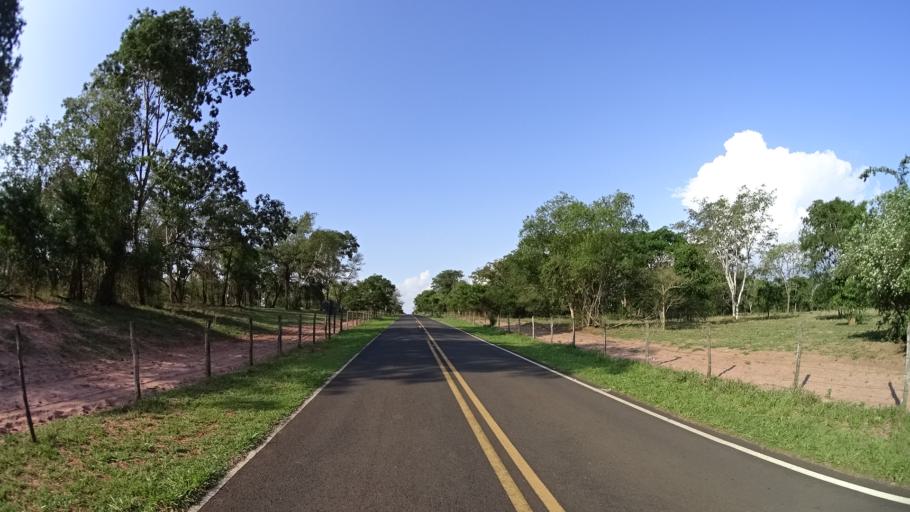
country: BR
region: Sao Paulo
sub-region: Urupes
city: Urupes
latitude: -21.4012
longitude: -49.5160
